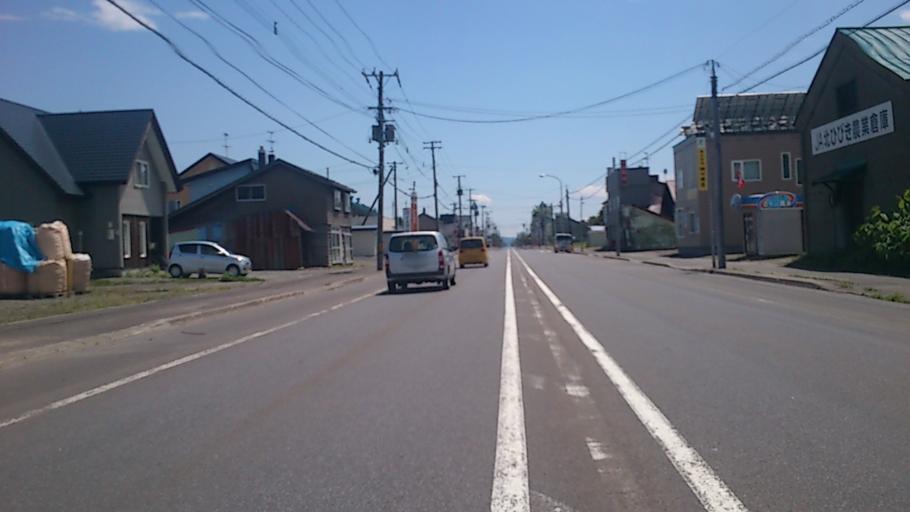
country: JP
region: Hokkaido
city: Nayoro
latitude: 44.2436
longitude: 142.3949
